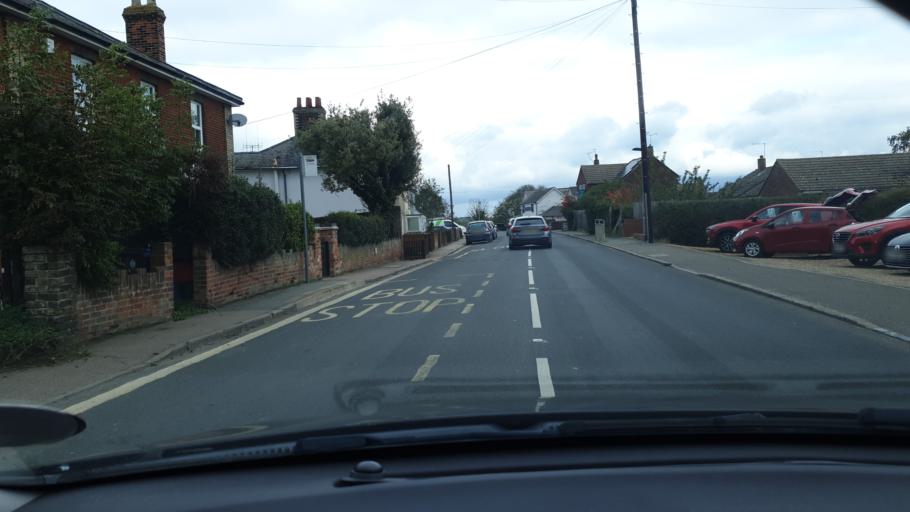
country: GB
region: England
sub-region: Essex
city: Mistley
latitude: 51.9424
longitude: 1.0864
